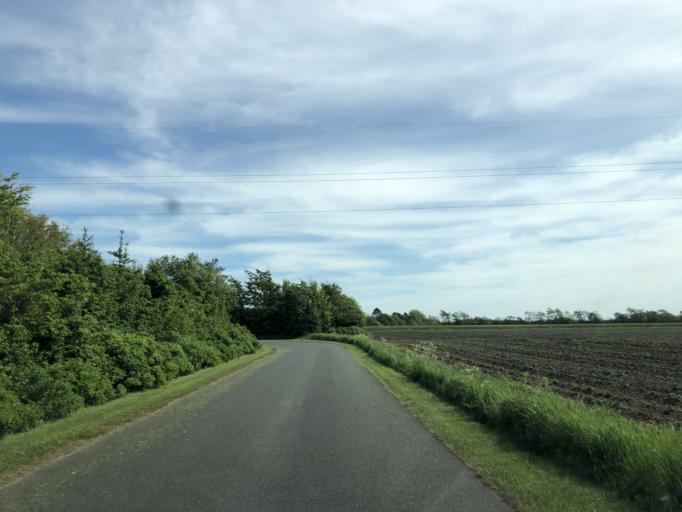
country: DK
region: Central Jutland
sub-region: Holstebro Kommune
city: Ulfborg
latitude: 56.2799
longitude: 8.2660
